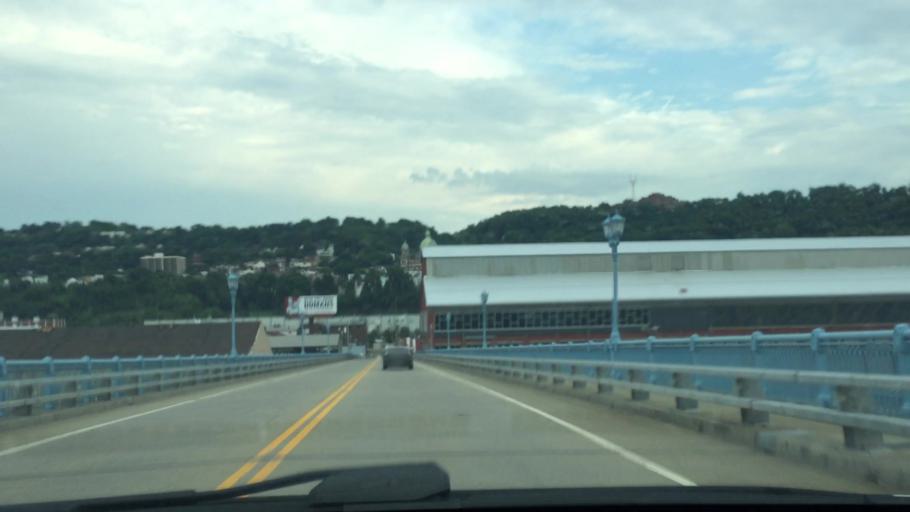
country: US
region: Pennsylvania
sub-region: Allegheny County
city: Millvale
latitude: 40.4620
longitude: -79.9741
